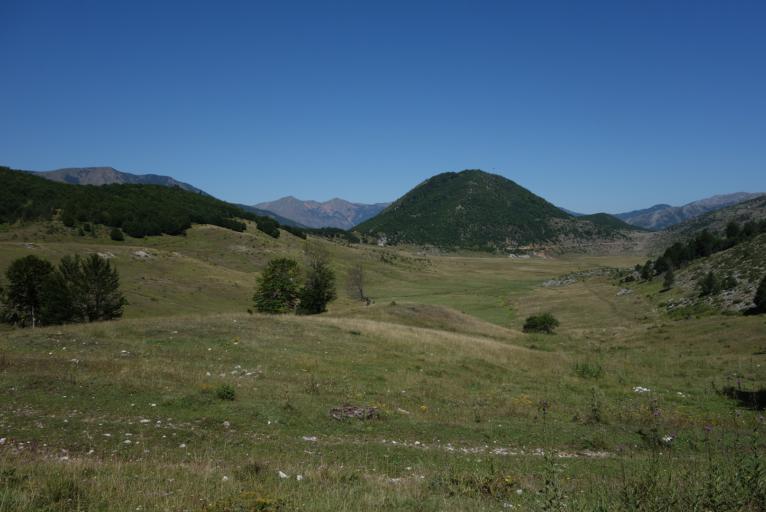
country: AL
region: Diber
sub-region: Rrethi i Bulqizes
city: Zerqan
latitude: 41.4612
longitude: 20.3579
